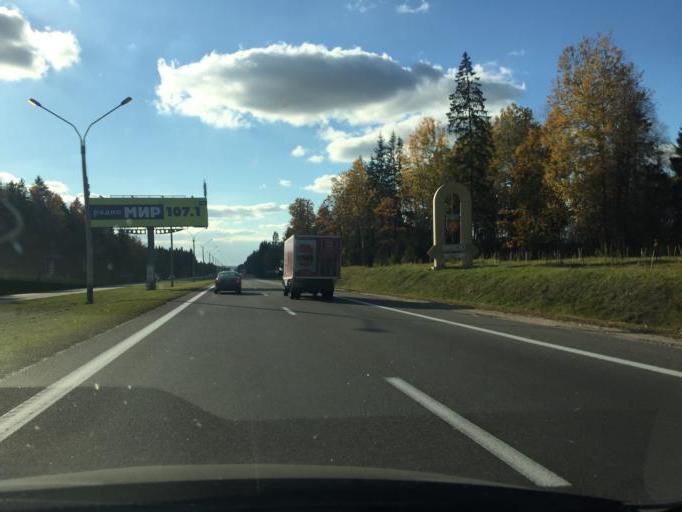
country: BY
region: Minsk
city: Slabada
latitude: 54.0067
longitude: 27.8484
